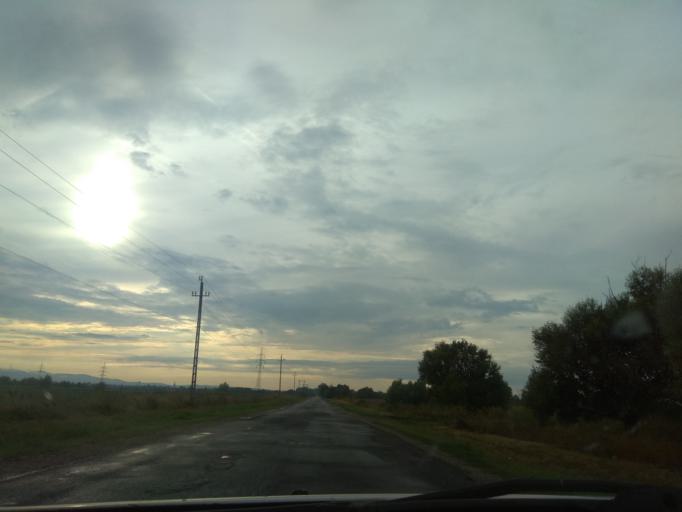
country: HU
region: Borsod-Abauj-Zemplen
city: Onga
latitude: 48.1148
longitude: 20.9413
